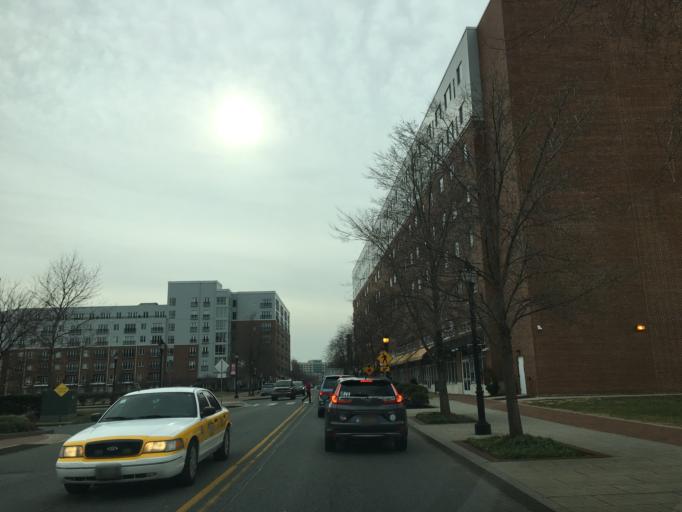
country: US
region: Delaware
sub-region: New Castle County
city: Wilmington
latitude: 39.7374
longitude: -75.5594
